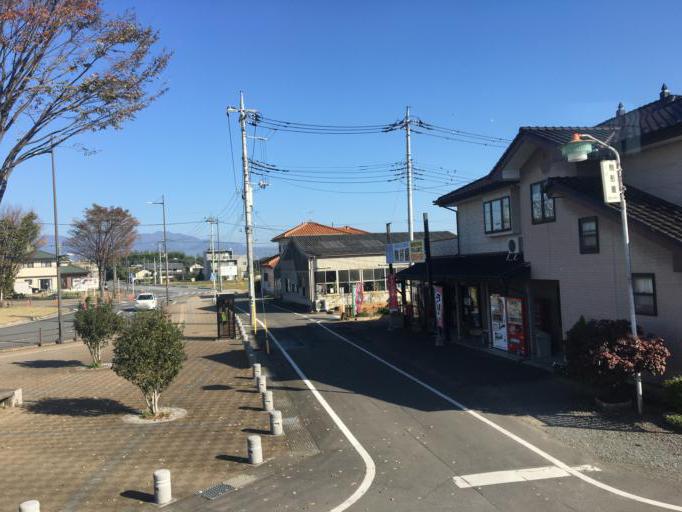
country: JP
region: Gunma
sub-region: Sawa-gun
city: Tamamura
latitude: 36.3538
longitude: 139.1405
